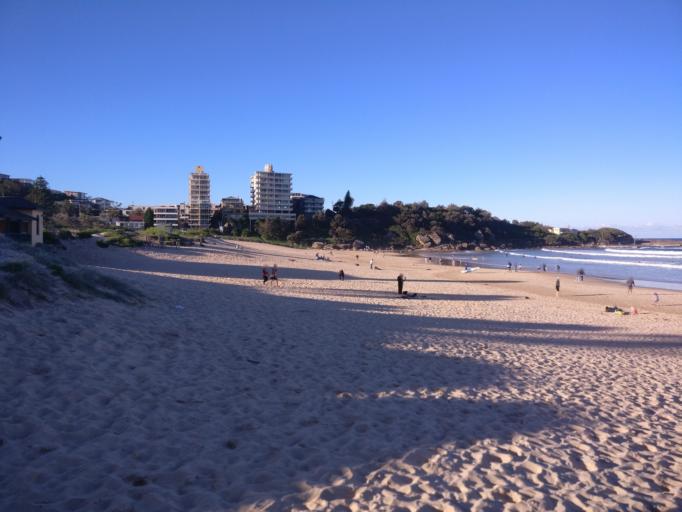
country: AU
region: New South Wales
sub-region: Warringah
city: Freshwater
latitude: -33.7816
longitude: 151.2897
